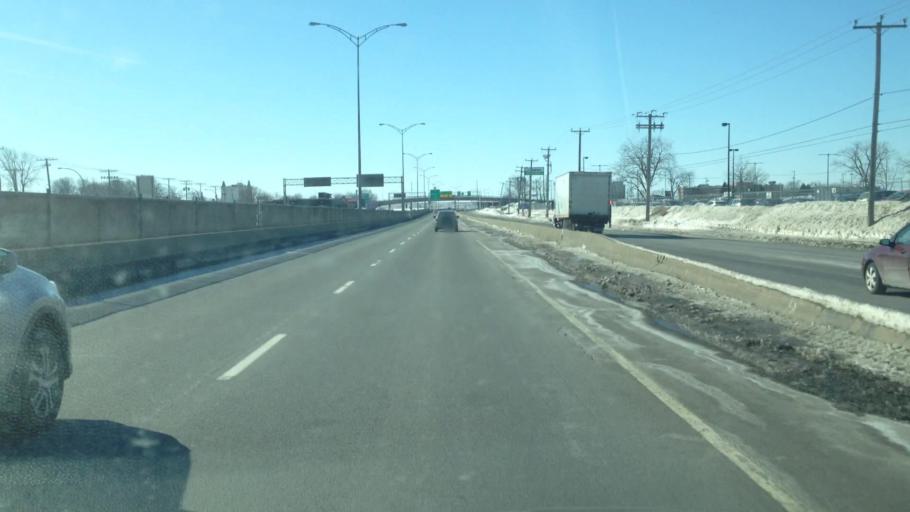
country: CA
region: Quebec
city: Dorval
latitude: 45.4564
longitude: -73.7322
